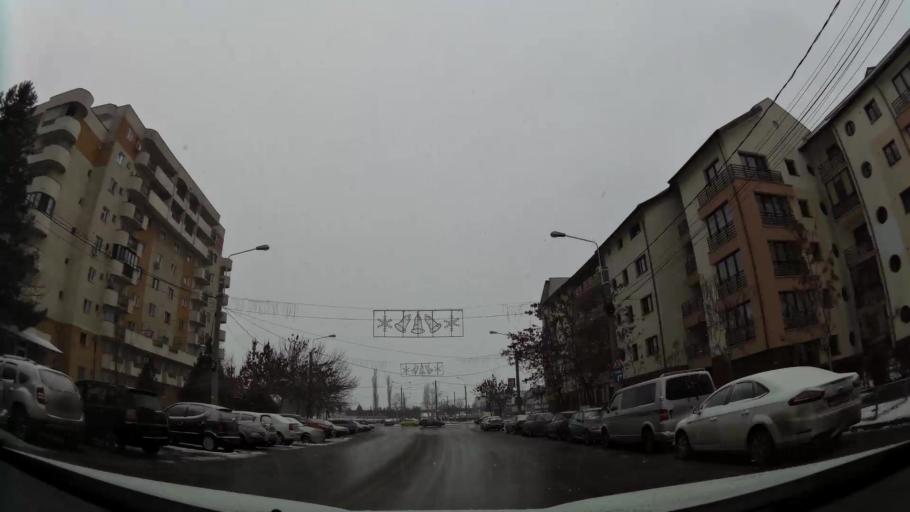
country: RO
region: Prahova
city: Ploiesti
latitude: 44.9270
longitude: 25.9963
